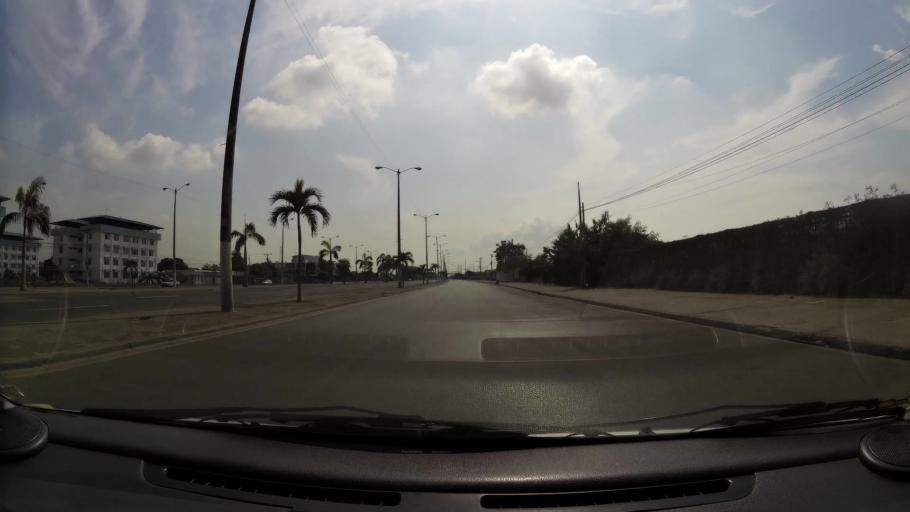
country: EC
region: Guayas
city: Guayaquil
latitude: -2.2738
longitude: -79.9045
